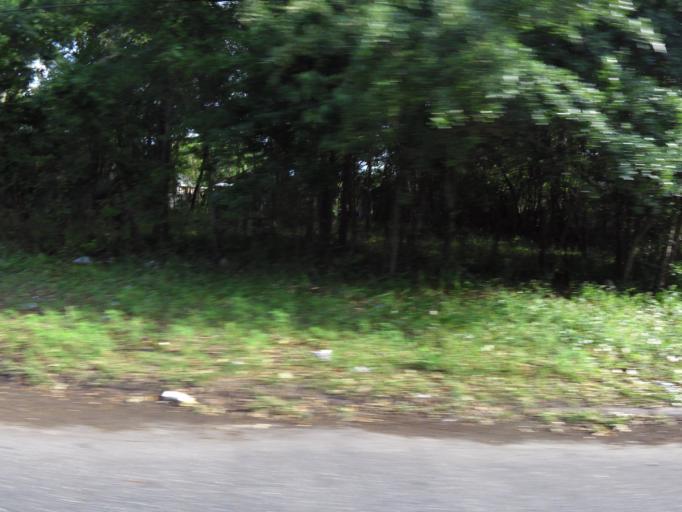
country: US
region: Florida
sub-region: Duval County
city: Jacksonville
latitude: 30.3704
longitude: -81.6580
